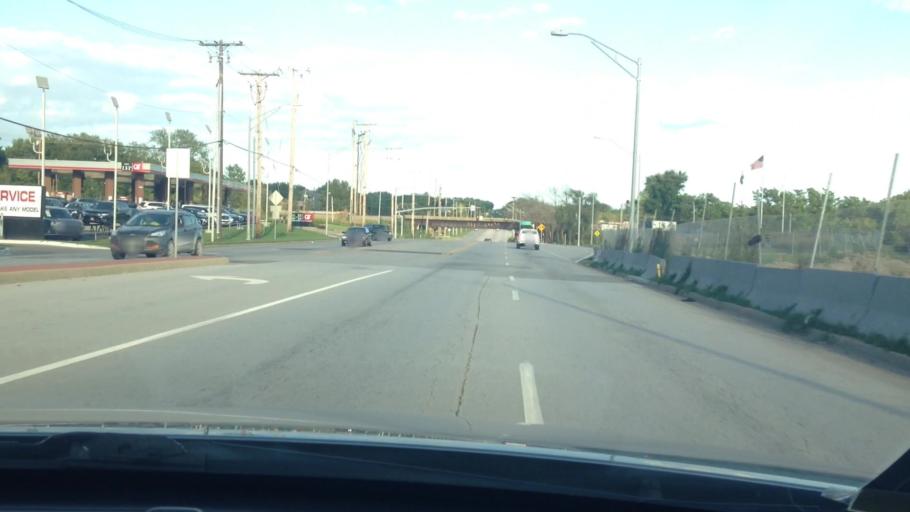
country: US
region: Missouri
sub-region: Jackson County
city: Raytown
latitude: 38.9672
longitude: -94.5172
